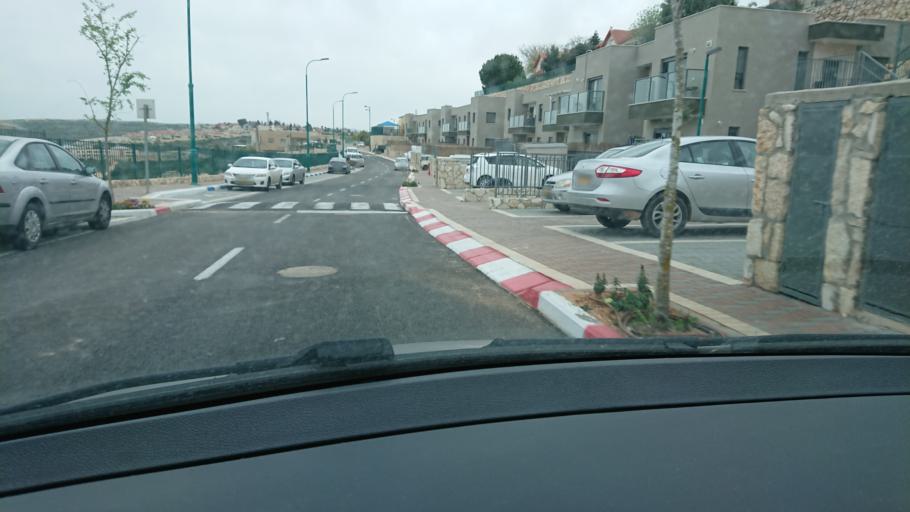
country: PS
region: West Bank
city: Rafat
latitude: 32.0643
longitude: 35.0529
